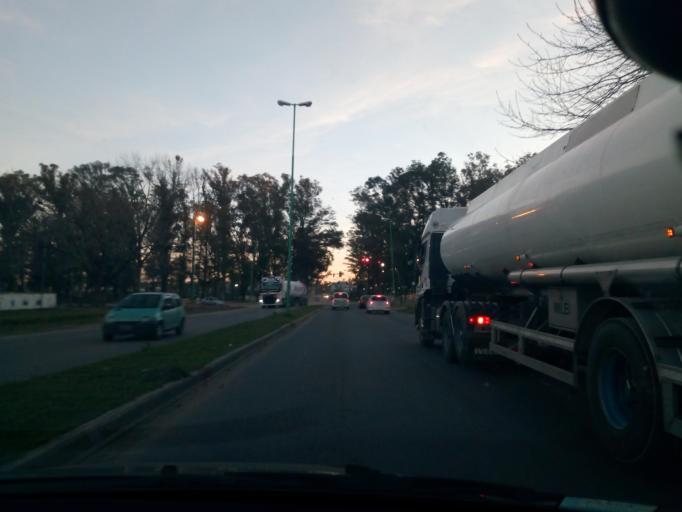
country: AR
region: Buenos Aires
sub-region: Partido de La Plata
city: La Plata
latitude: -34.8927
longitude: -57.9376
